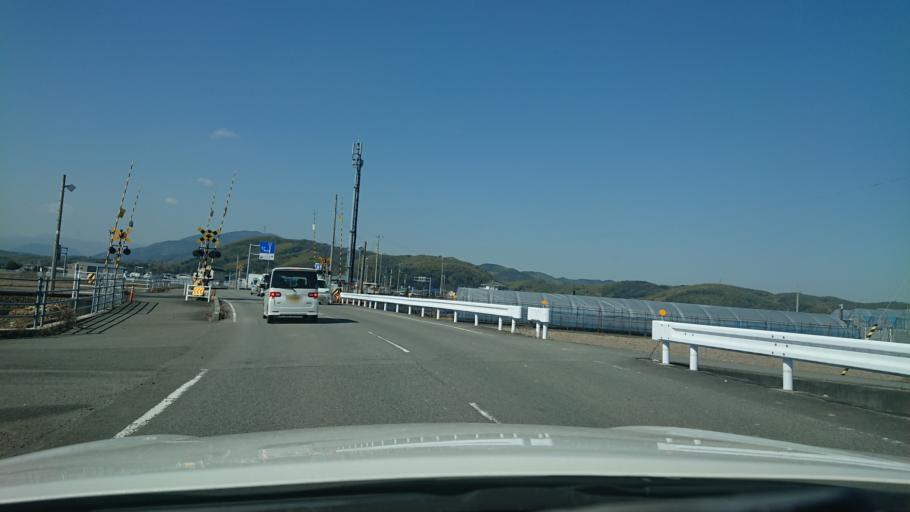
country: JP
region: Tokushima
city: Komatsushimacho
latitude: 33.9651
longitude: 134.6140
